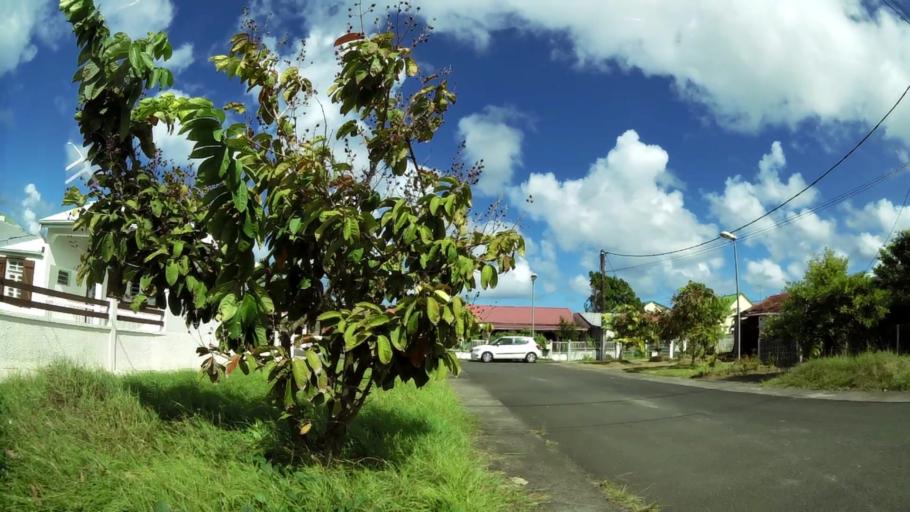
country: GP
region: Guadeloupe
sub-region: Guadeloupe
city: Port-Louis
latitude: 16.4215
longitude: -61.5306
